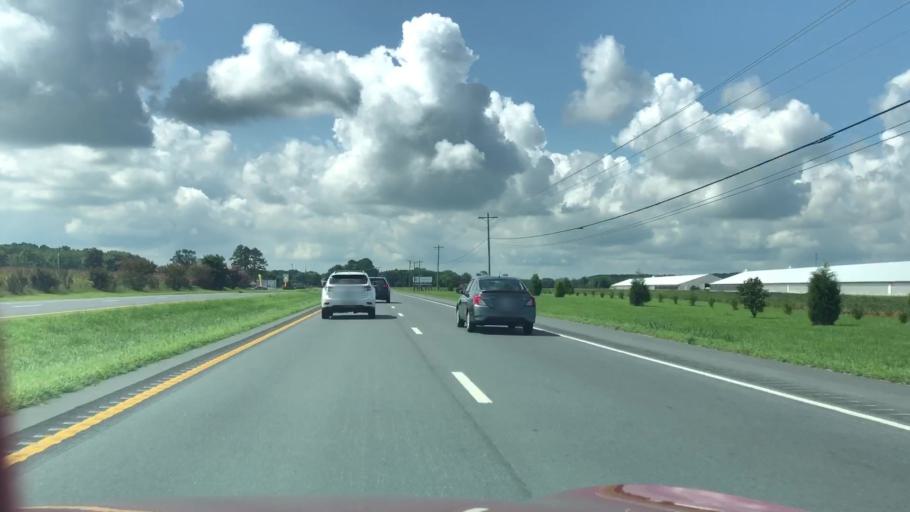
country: US
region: Virginia
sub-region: Accomack County
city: Accomac
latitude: 37.7822
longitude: -75.6092
